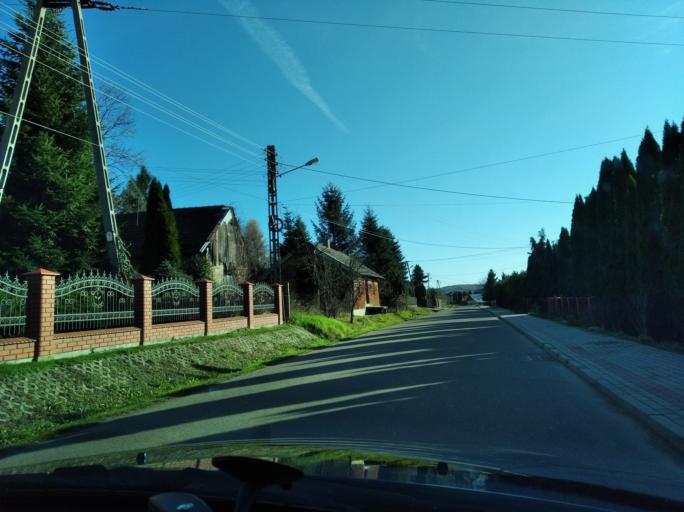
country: PL
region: Subcarpathian Voivodeship
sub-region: Powiat rzeszowski
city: Lutoryz
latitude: 49.9663
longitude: 21.9135
